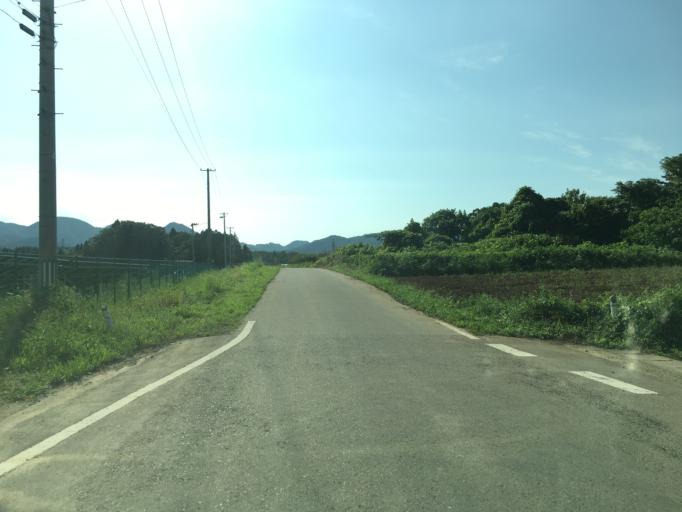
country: JP
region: Miyagi
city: Marumori
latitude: 37.8234
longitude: 140.9073
